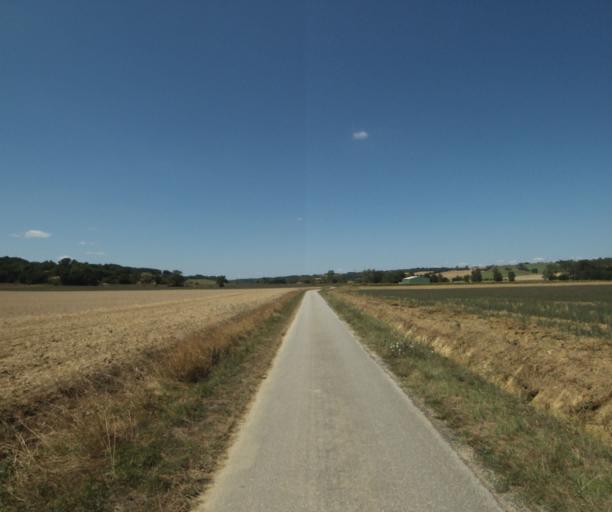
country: FR
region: Midi-Pyrenees
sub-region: Departement de la Haute-Garonne
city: Saint-Felix-Lauragais
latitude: 43.4810
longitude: 1.8768
